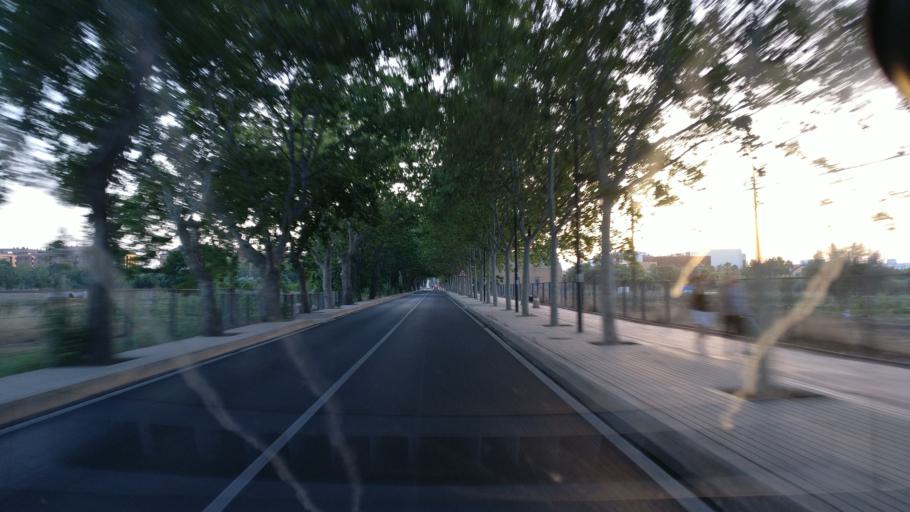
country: ES
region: Valencia
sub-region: Provincia de Valencia
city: Aldaia
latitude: 39.4638
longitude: -0.4523
